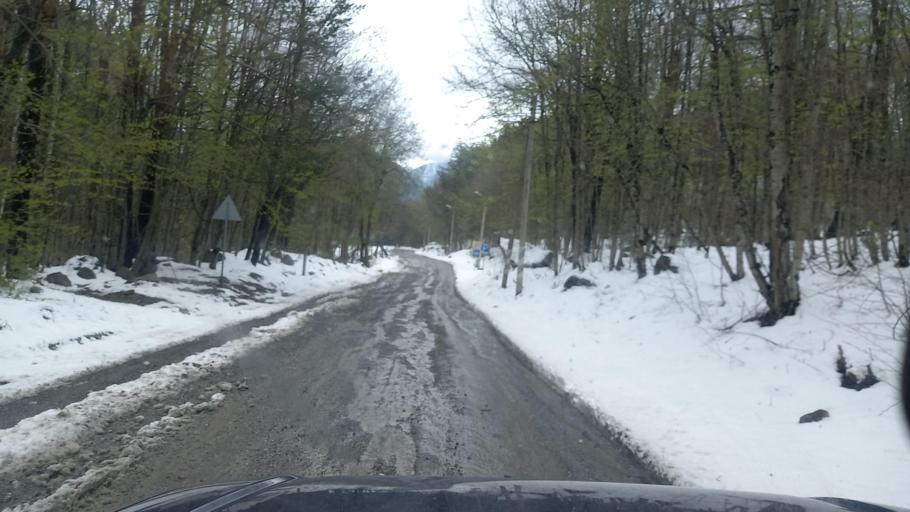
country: RU
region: North Ossetia
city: Mizur
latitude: 42.7892
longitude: 43.9037
